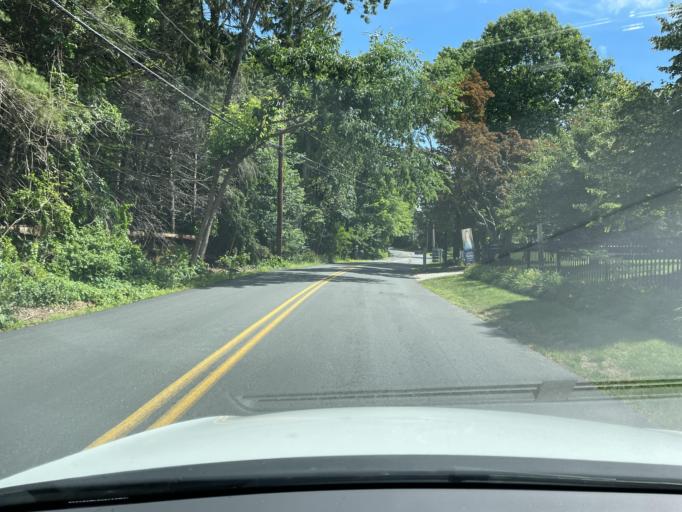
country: US
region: Massachusetts
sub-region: Essex County
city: Andover
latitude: 42.6528
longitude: -71.1248
